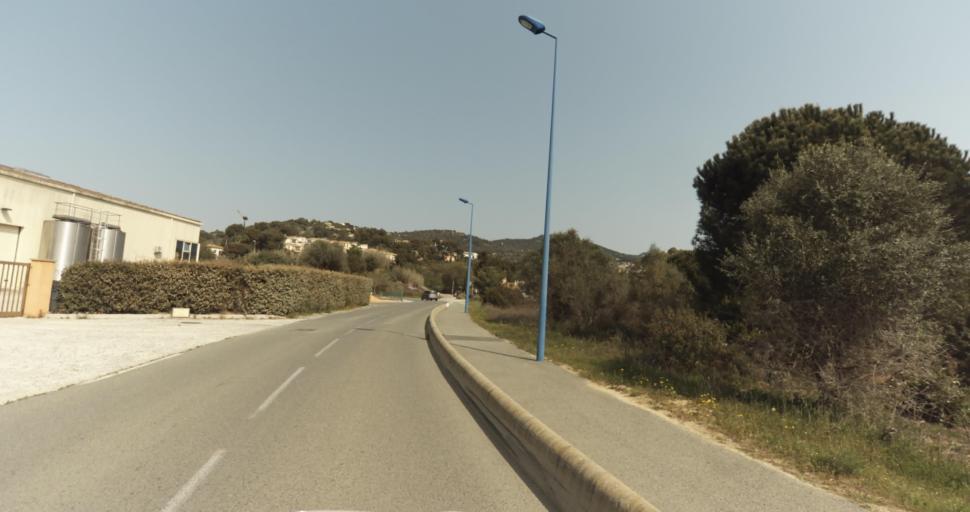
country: FR
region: Provence-Alpes-Cote d'Azur
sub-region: Departement du Var
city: Bormes-les-Mimosas
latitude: 43.1406
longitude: 6.3326
